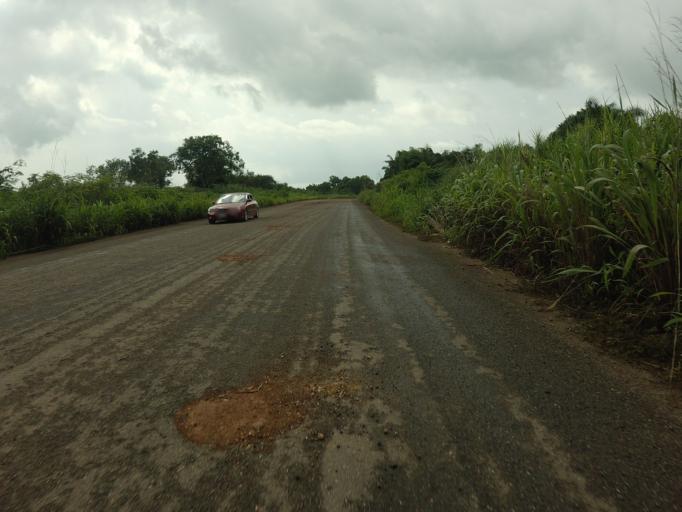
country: TG
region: Plateaux
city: Kpalime
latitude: 6.9412
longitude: 0.4618
